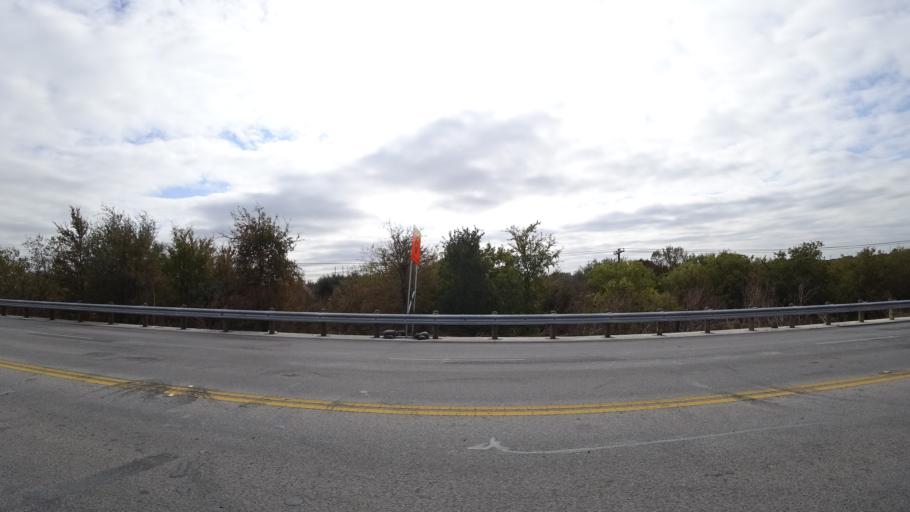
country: US
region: Texas
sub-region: Williamson County
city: Round Rock
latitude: 30.5346
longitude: -97.7000
